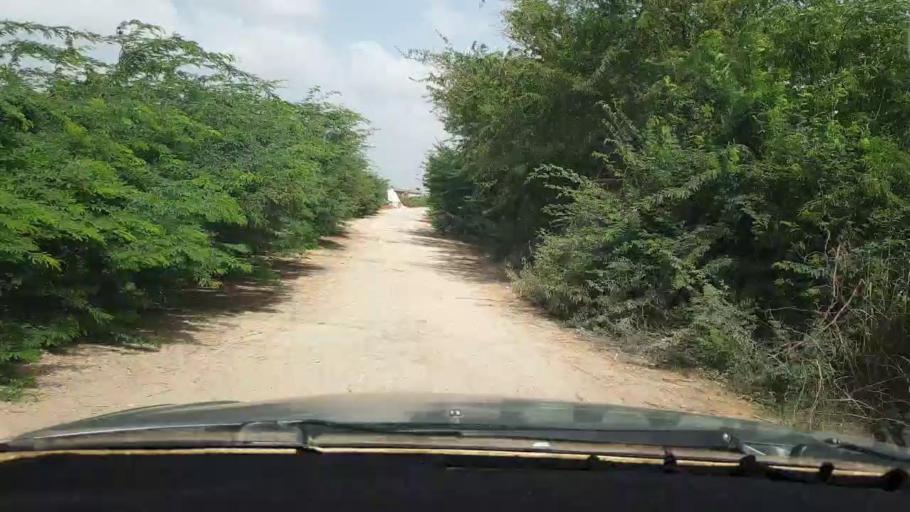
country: PK
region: Sindh
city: Tando Bago
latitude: 24.7564
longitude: 69.1926
